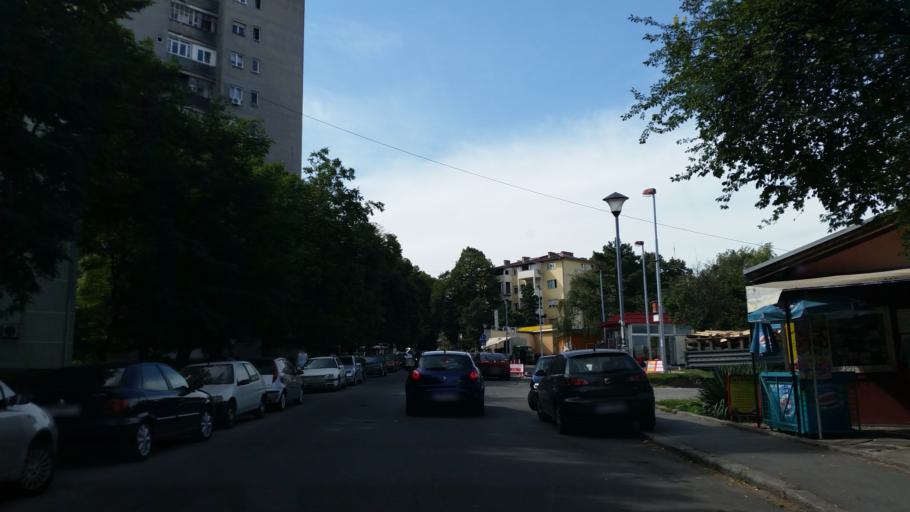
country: RS
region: Central Serbia
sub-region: Belgrade
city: Palilula
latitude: 44.8163
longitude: 20.5193
